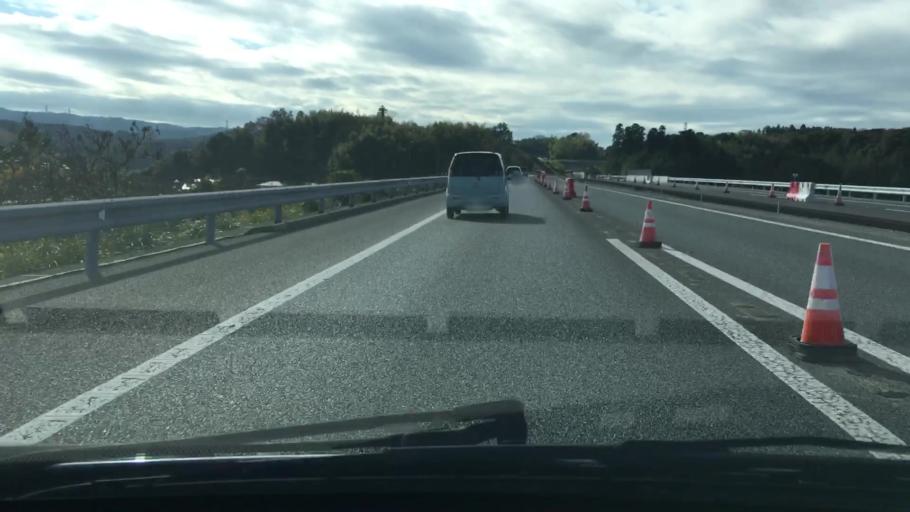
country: JP
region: Chiba
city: Kimitsu
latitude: 35.3061
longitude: 139.9418
